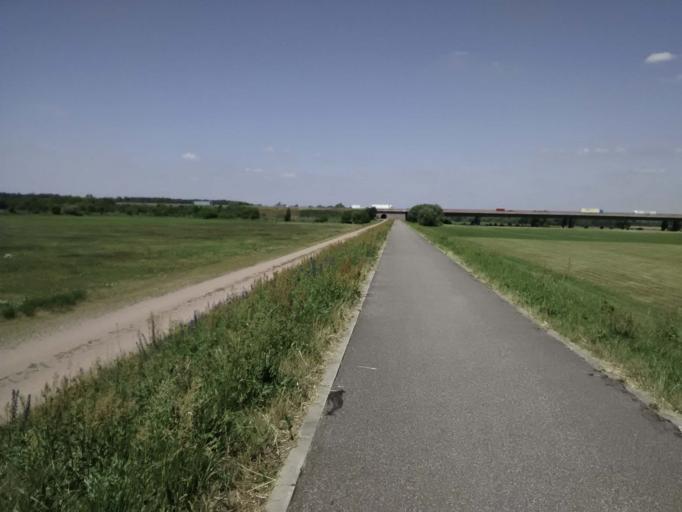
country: DE
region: Saxony-Anhalt
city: Vockerode
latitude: 51.8537
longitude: 12.3512
